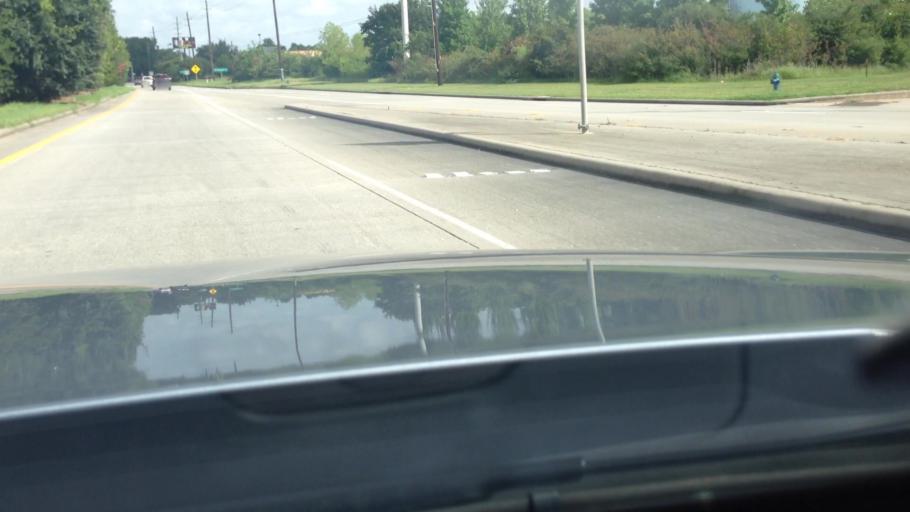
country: US
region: Texas
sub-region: Harris County
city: Hudson
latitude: 29.9516
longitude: -95.5348
